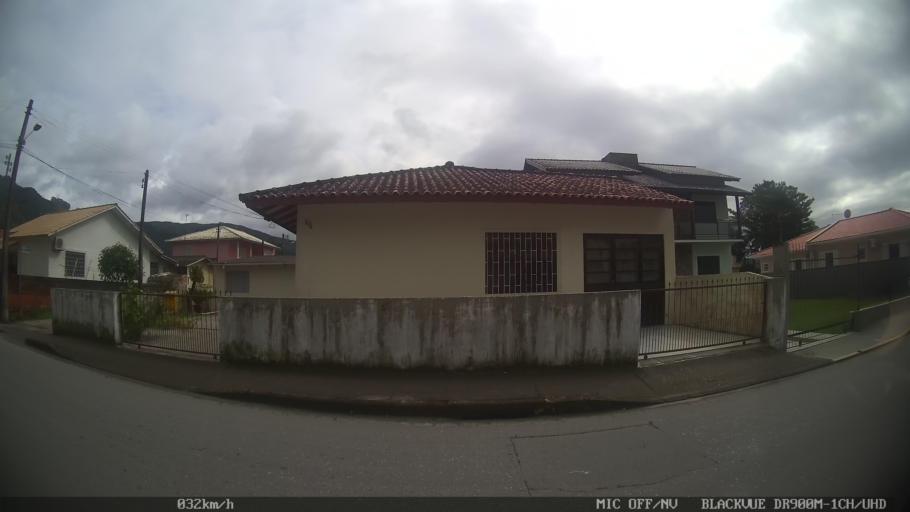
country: BR
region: Santa Catarina
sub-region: Biguacu
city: Biguacu
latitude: -27.5166
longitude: -48.6541
